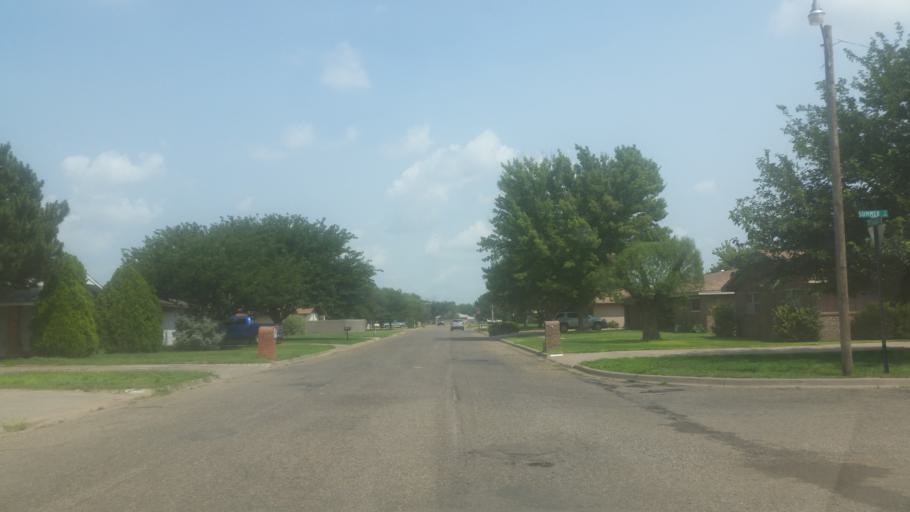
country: US
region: New Mexico
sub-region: Curry County
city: Clovis
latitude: 34.4182
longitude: -103.2269
